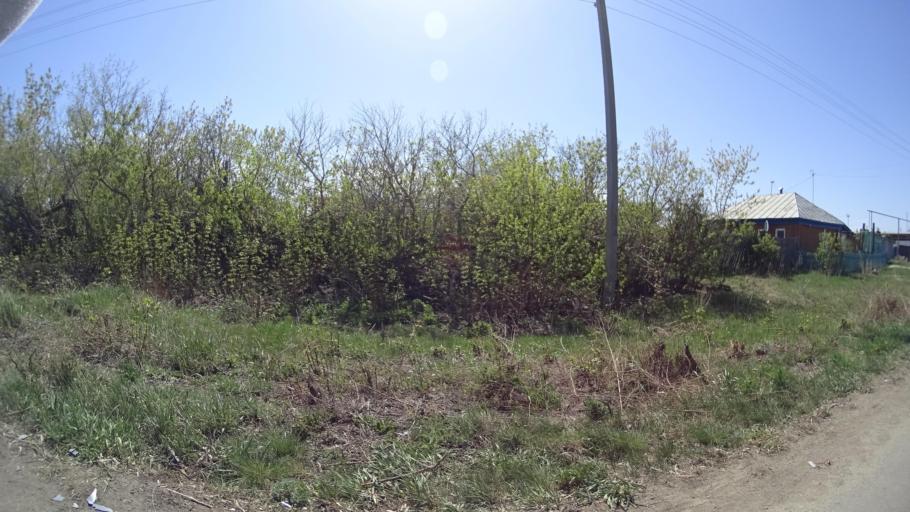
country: RU
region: Chelyabinsk
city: Chesma
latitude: 53.7937
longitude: 61.0348
